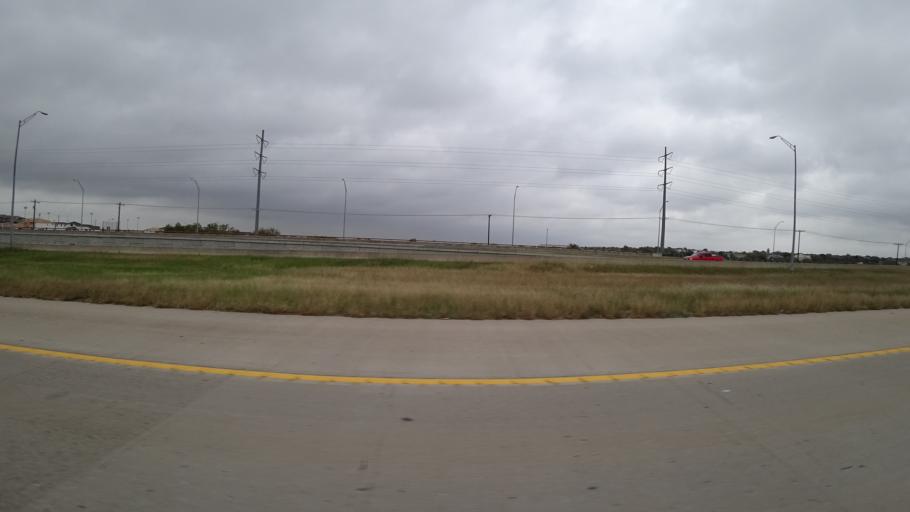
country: US
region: Texas
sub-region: Travis County
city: Windemere
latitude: 30.4885
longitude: -97.6332
